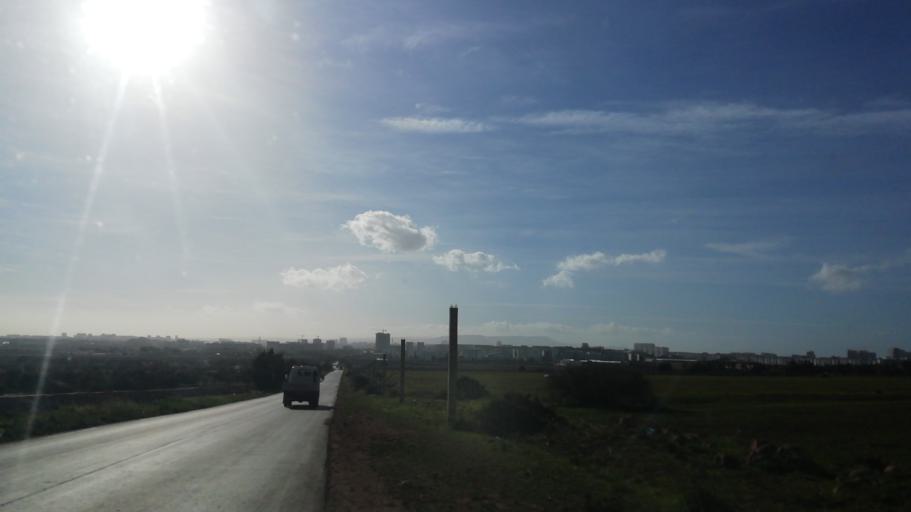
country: DZ
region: Oran
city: Bir el Djir
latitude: 35.7524
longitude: -0.5158
